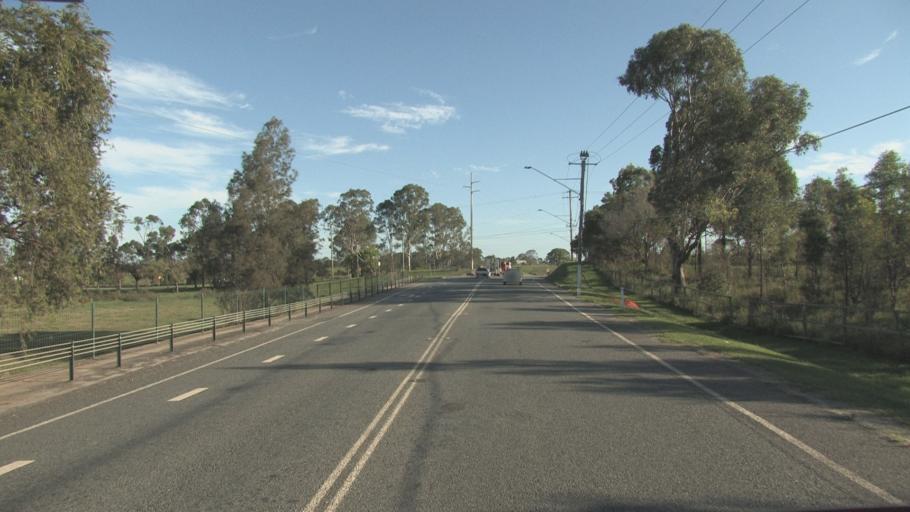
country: AU
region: Queensland
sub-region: Logan
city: Waterford West
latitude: -27.6987
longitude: 153.1181
